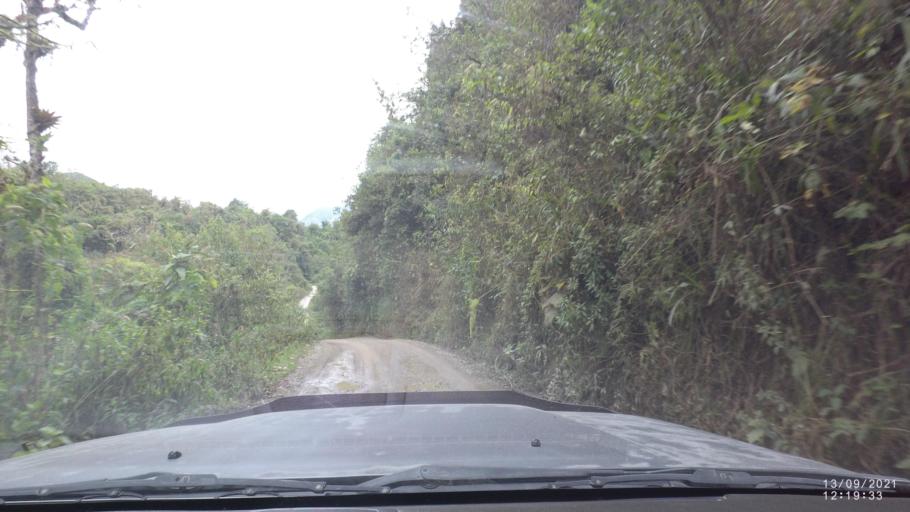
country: BO
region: Cochabamba
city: Colomi
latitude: -17.2340
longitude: -65.8193
